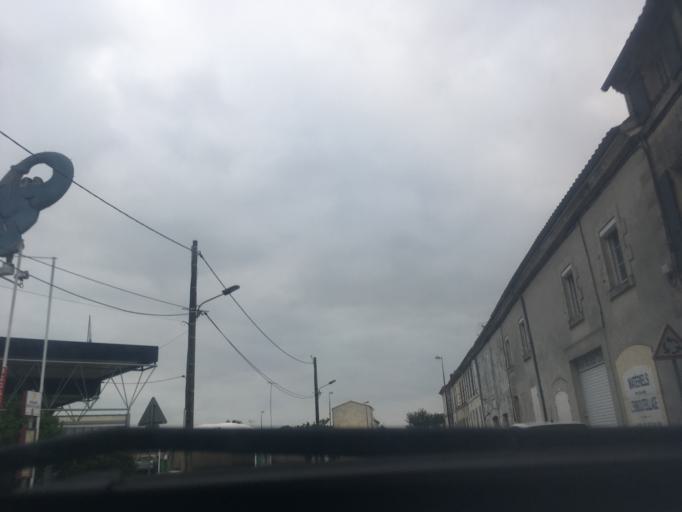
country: FR
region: Poitou-Charentes
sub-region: Departement de la Charente
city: Cognac
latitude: 45.6840
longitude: -0.3288
